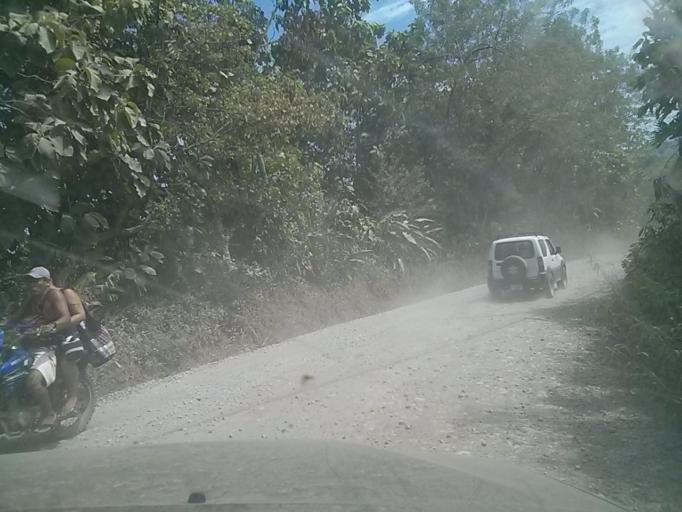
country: CR
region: Puntarenas
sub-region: Canton de Golfito
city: Golfito
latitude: 8.4552
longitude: -83.0510
